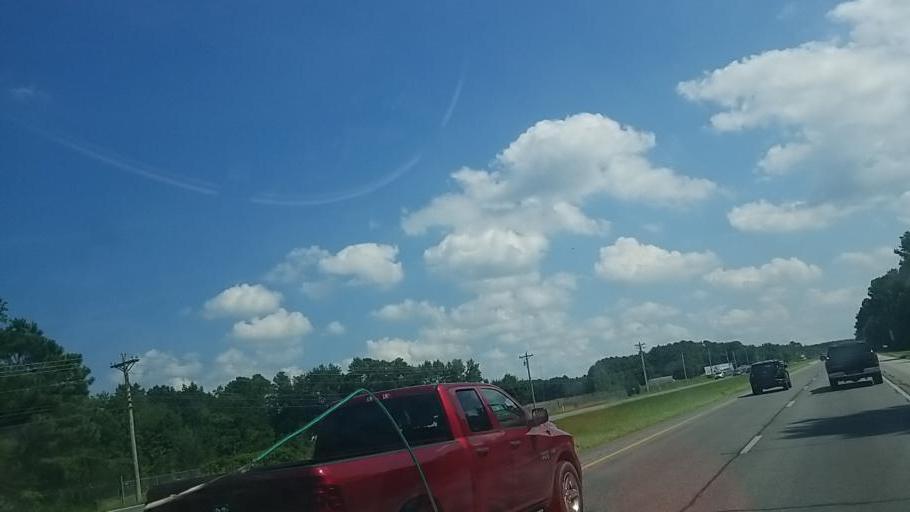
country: US
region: Delaware
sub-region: Sussex County
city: Georgetown
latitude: 38.7251
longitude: -75.4129
